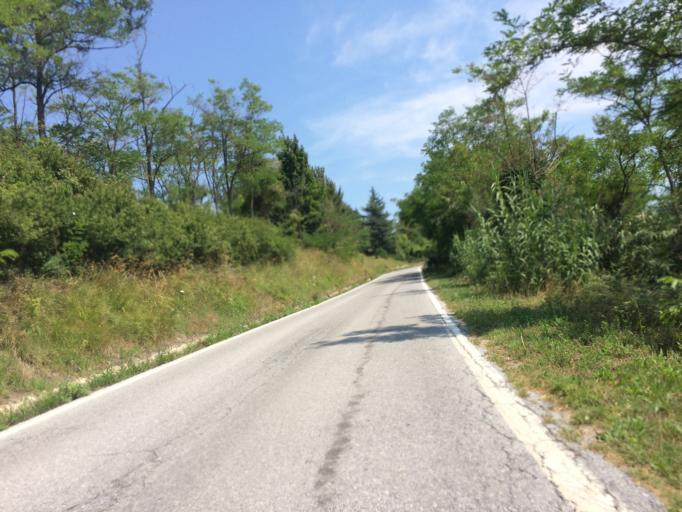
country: IT
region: Piedmont
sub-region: Provincia di Cuneo
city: Serravalle Langhe
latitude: 44.5594
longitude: 8.0477
